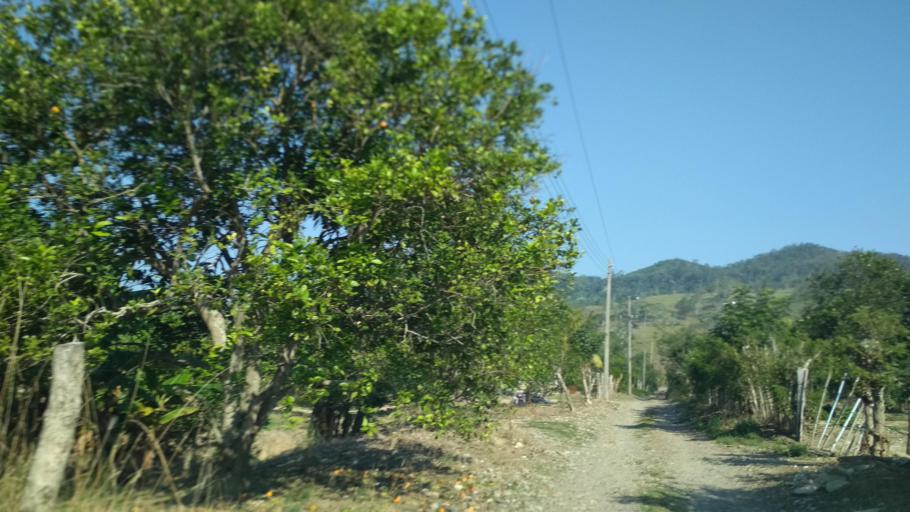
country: MX
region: Veracruz
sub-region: Papantla
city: Polutla
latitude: 20.4594
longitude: -97.2080
